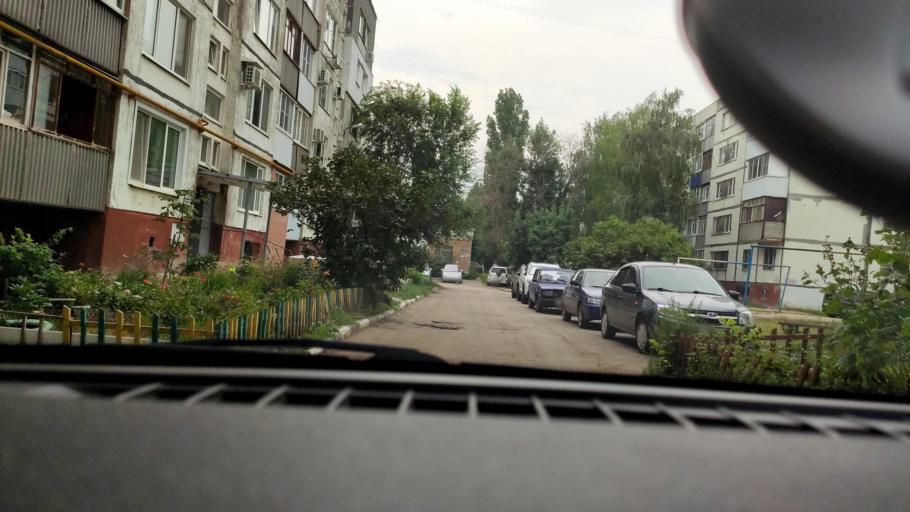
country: RU
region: Samara
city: Novokuybyshevsk
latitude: 53.0926
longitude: 49.9908
